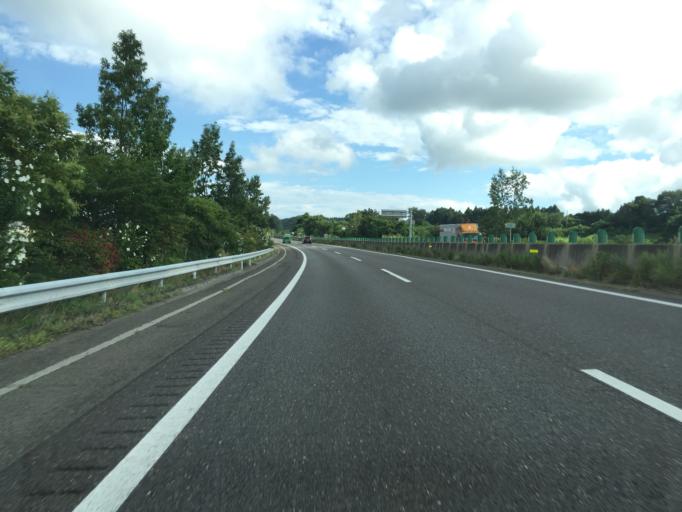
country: JP
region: Fukushima
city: Nihommatsu
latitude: 37.6121
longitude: 140.4230
